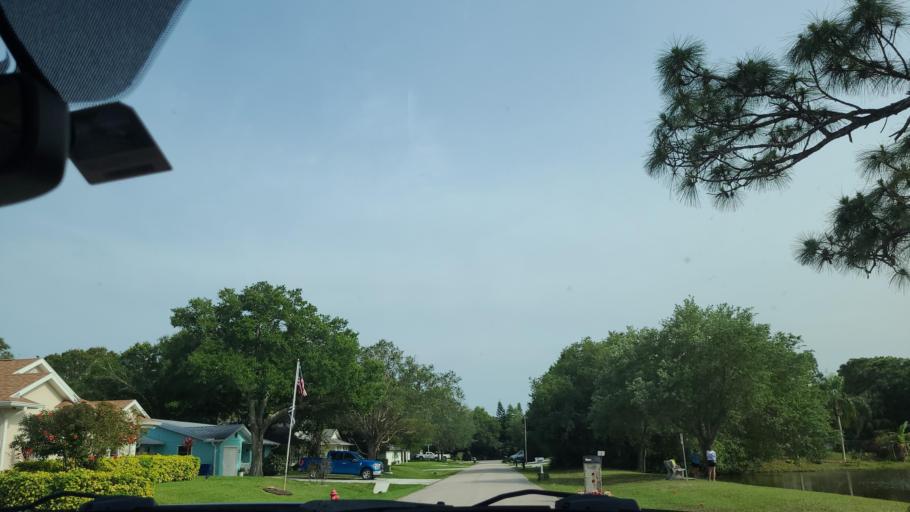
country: US
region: Florida
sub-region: Indian River County
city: Sebastian
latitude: 27.7660
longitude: -80.4894
